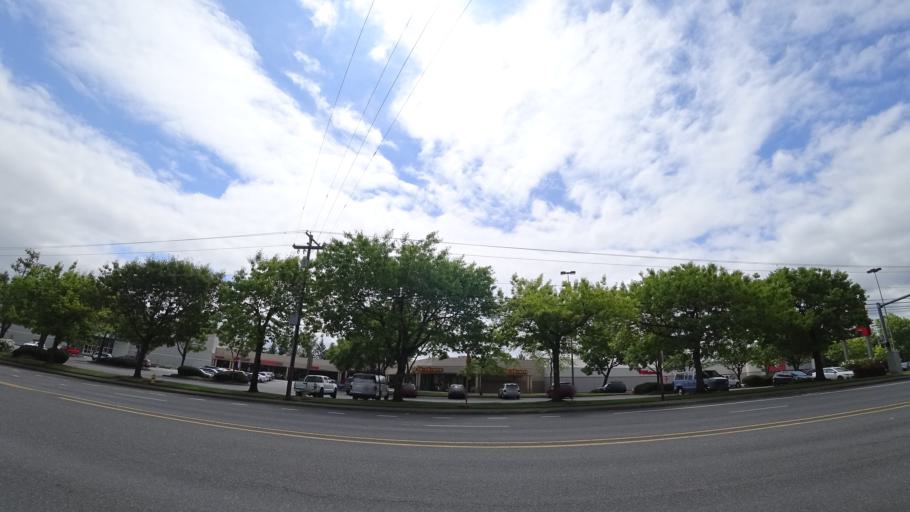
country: US
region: Oregon
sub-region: Washington County
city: Metzger
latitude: 45.4545
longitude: -122.7777
